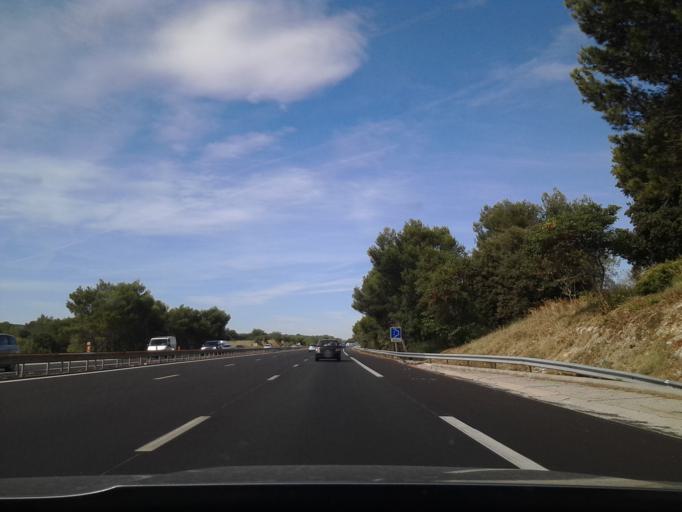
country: FR
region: Languedoc-Roussillon
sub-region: Departement de l'Herault
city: Fabregues
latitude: 43.5270
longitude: 3.7679
